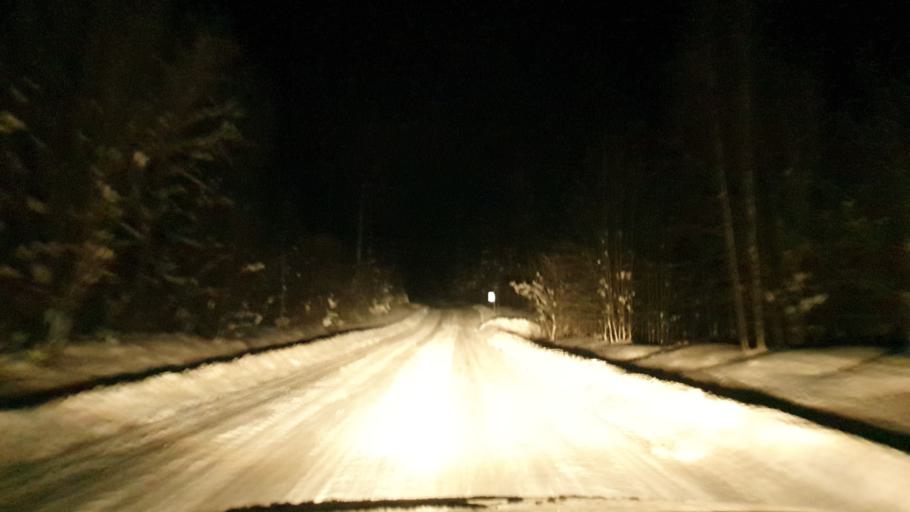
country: EE
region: Vorumaa
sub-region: Antsla vald
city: Vana-Antsla
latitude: 57.9462
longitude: 26.6132
